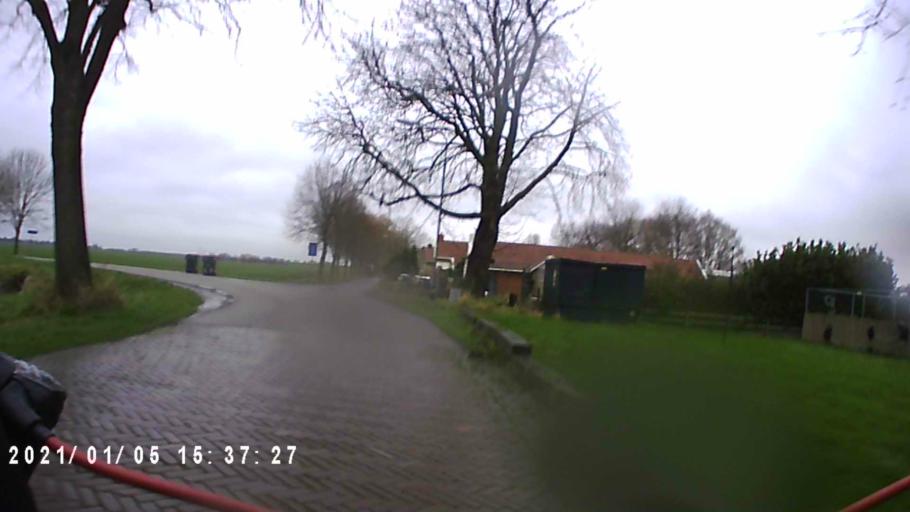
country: DE
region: Lower Saxony
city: Bunde
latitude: 53.2136
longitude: 7.1621
